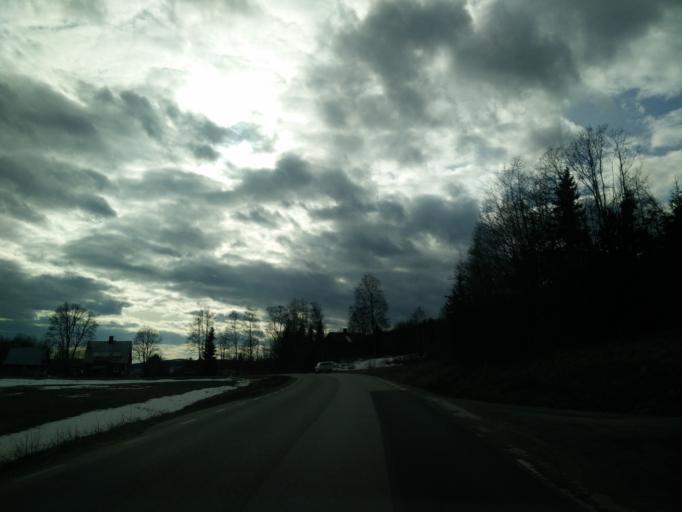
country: SE
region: Vaesternorrland
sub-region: Haernoesands Kommun
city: Haernoesand
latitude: 62.6820
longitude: 17.8814
